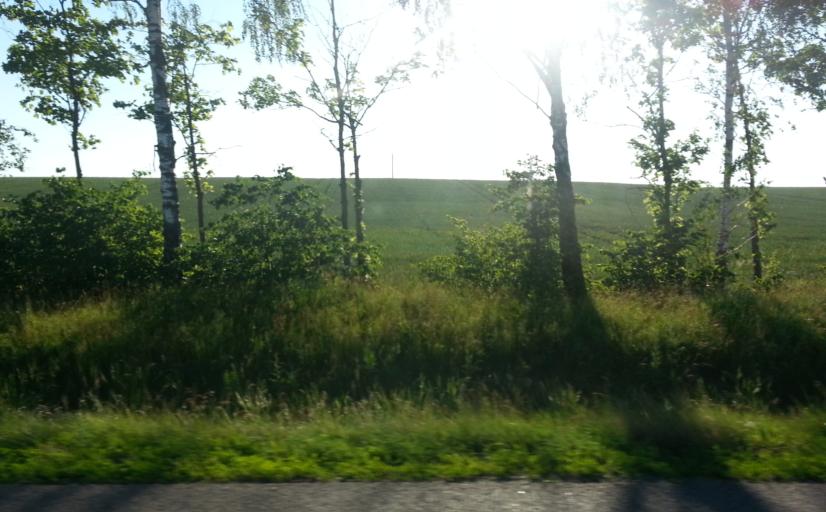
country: LT
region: Panevezys
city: Pasvalys
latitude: 55.9736
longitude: 24.3411
